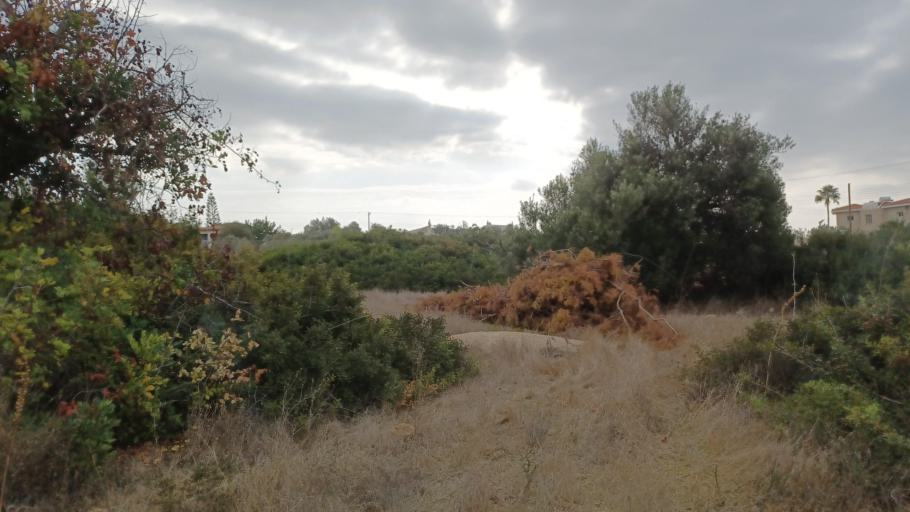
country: CY
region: Pafos
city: Pegeia
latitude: 34.8878
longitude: 32.3421
